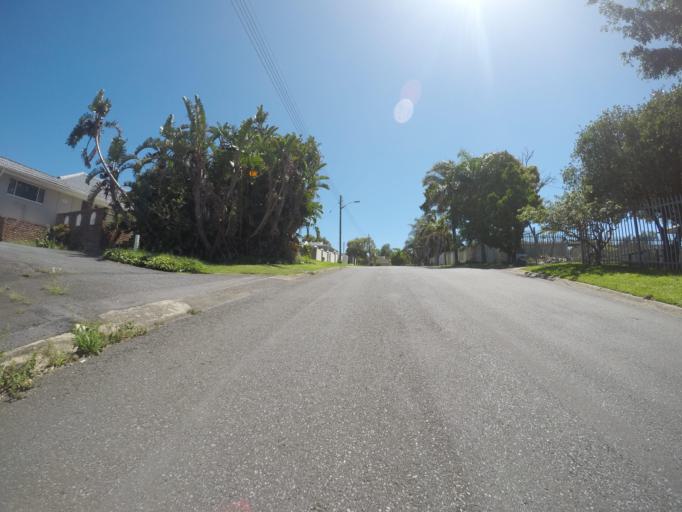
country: ZA
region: Eastern Cape
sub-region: Buffalo City Metropolitan Municipality
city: East London
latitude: -32.9716
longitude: 27.9476
